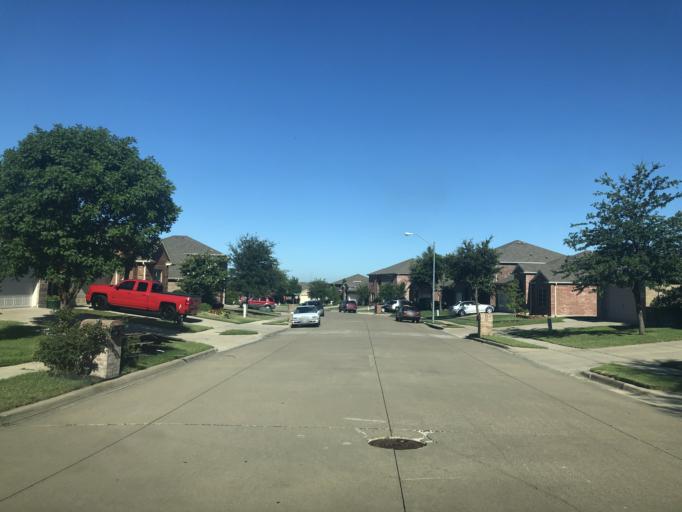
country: US
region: Texas
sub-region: Dallas County
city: Cedar Hill
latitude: 32.6463
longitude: -96.9724
